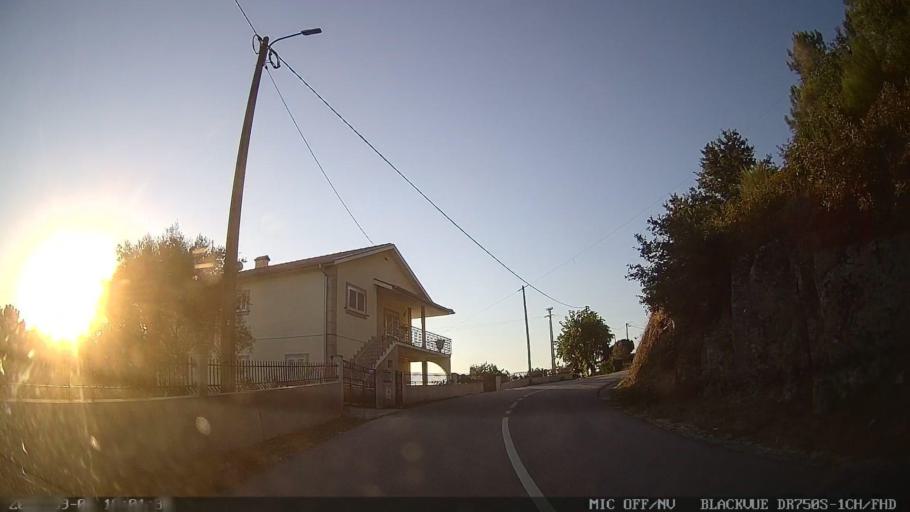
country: PT
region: Porto
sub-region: Baiao
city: Baiao
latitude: 41.2343
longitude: -7.9985
